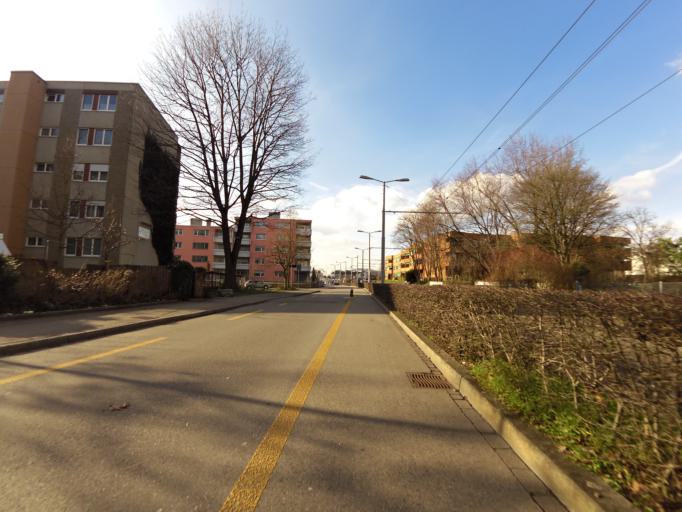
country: CH
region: Zurich
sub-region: Bezirk Zuerich
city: Zuerich (Kreis 9) / Altstetten
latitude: 47.3969
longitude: 8.4836
